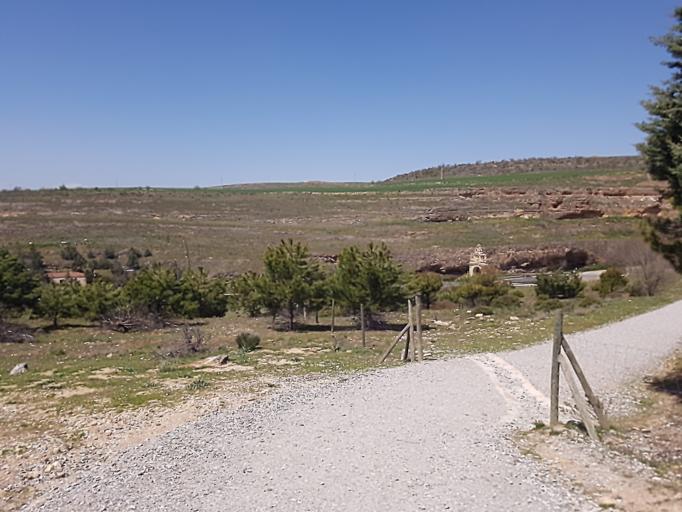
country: ES
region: Castille and Leon
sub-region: Provincia de Segovia
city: Segovia
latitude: 40.9536
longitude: -4.1360
